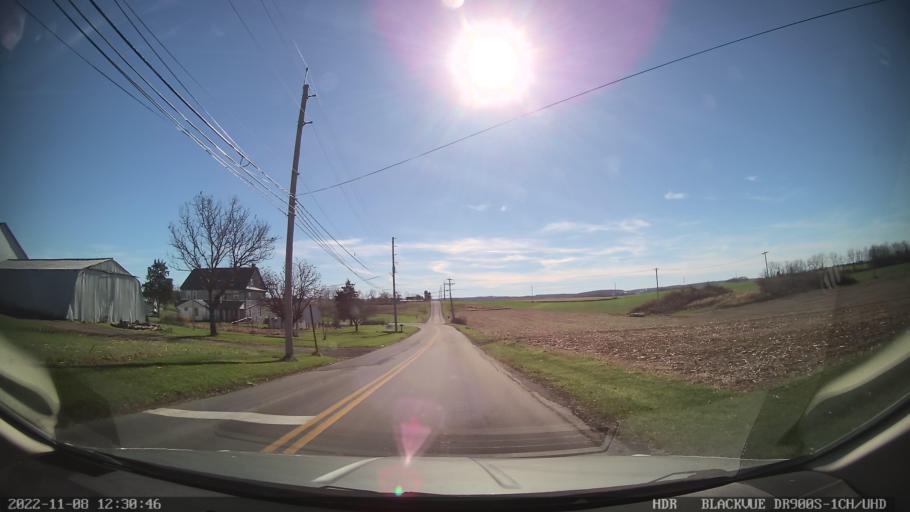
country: US
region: Pennsylvania
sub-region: Berks County
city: Kutztown
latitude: 40.5191
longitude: -75.7500
